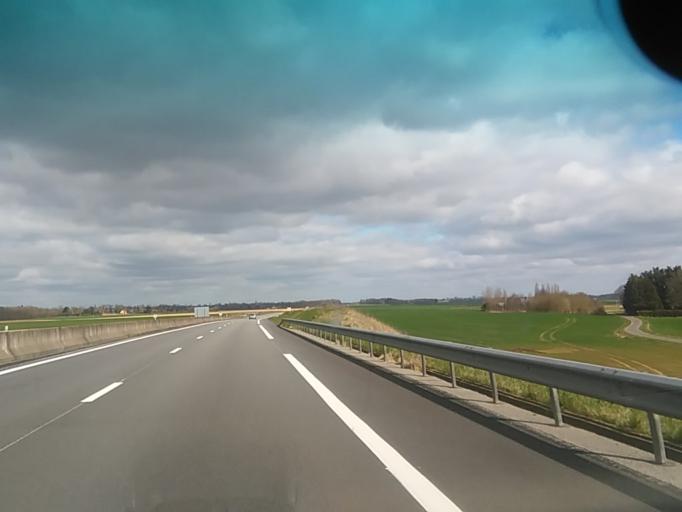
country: FR
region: Haute-Normandie
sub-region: Departement de l'Eure
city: Thiberville
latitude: 49.0794
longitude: 0.4782
